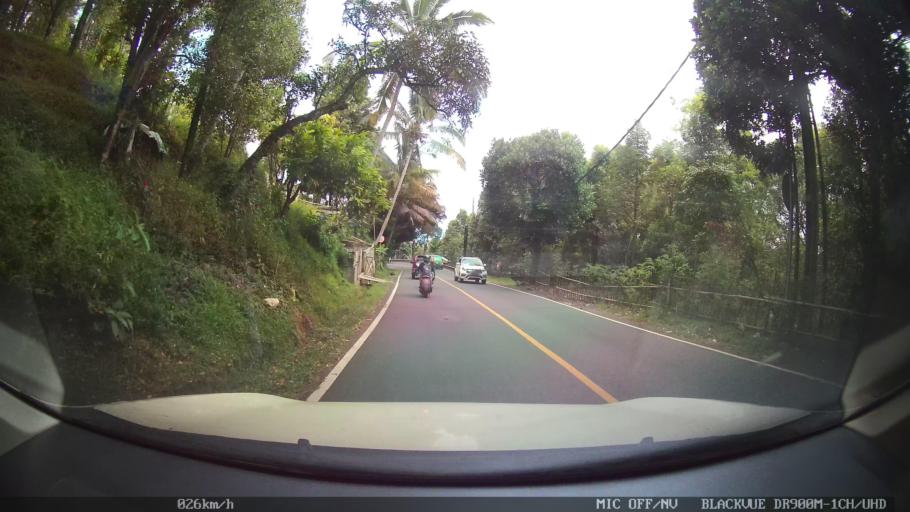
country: ID
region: Bali
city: Banjar Ambengan
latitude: -8.1957
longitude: 115.1406
